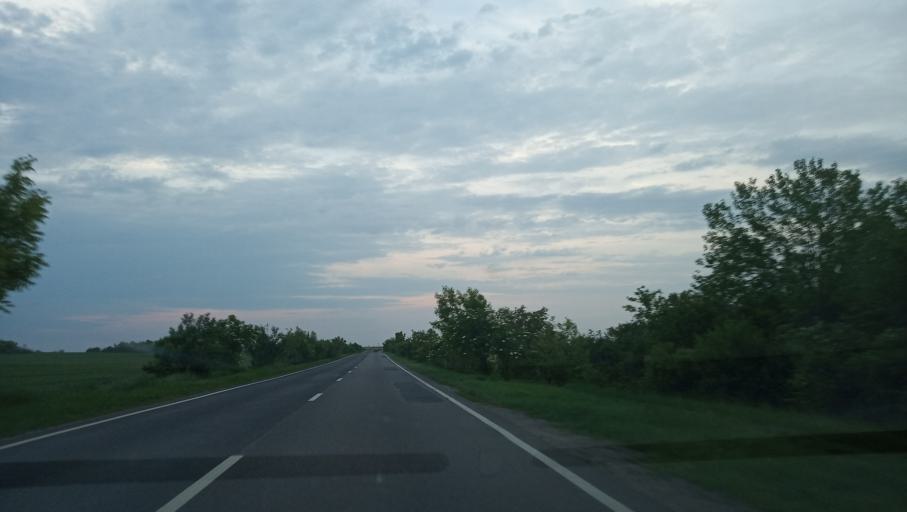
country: RO
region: Timis
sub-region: Comuna Voiteg
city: Voiteg
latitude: 45.4768
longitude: 21.2337
